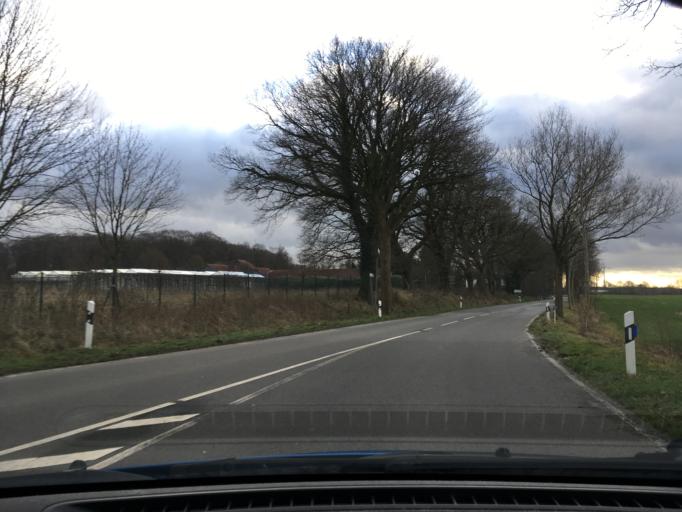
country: DE
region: Schleswig-Holstein
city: Christinenthal
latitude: 54.0523
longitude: 9.5315
